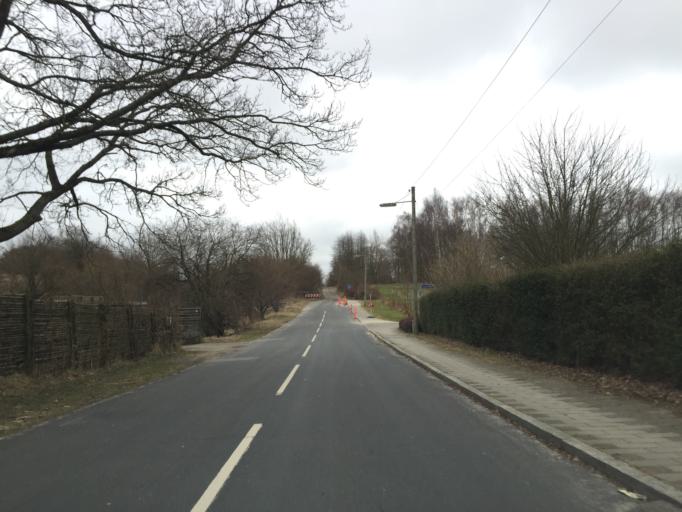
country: DK
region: Capital Region
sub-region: Allerod Kommune
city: Lillerod
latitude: 55.9031
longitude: 12.3300
